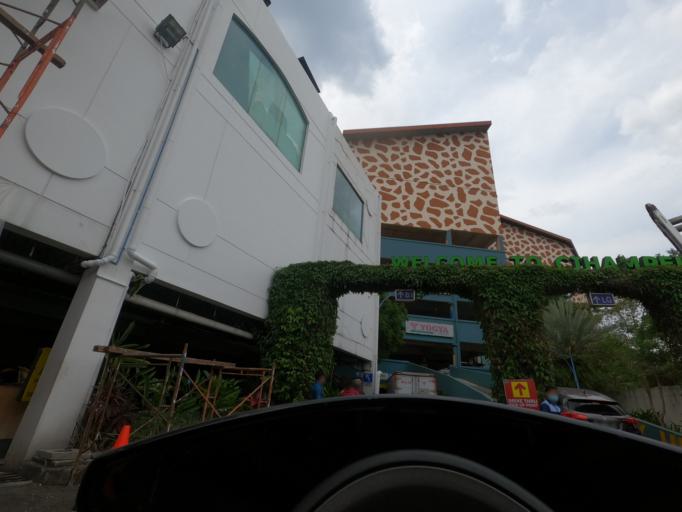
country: ID
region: West Java
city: Bandung
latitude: -6.8941
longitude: 107.6058
